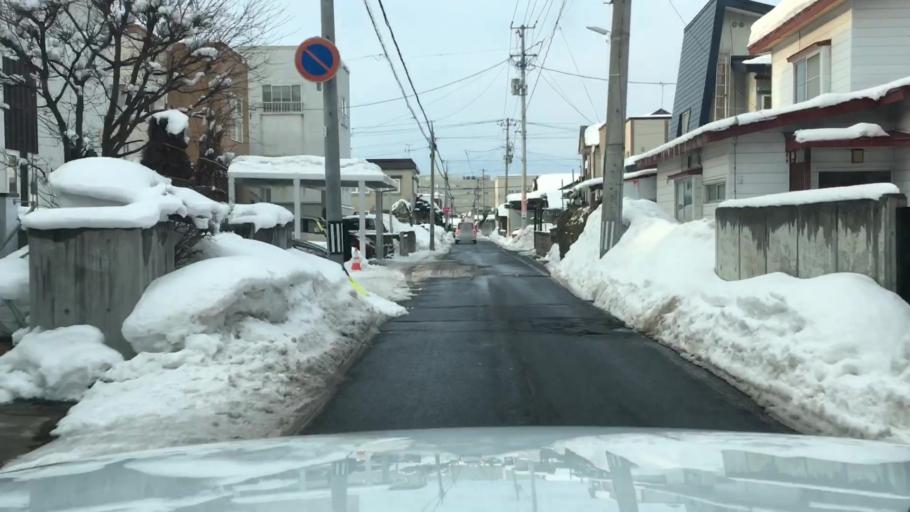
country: JP
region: Aomori
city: Hirosaki
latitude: 40.5853
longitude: 140.4793
